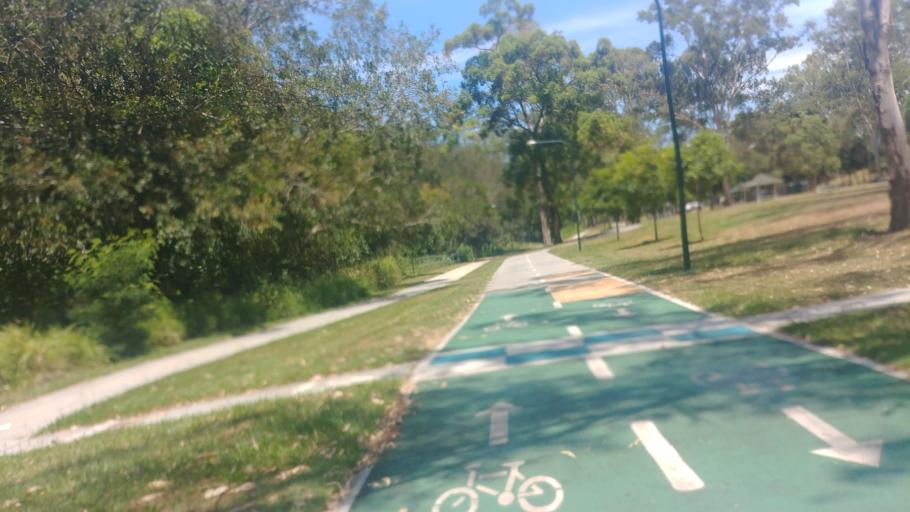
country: AU
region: Queensland
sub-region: Brisbane
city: Wavell Heights
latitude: -27.4049
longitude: 153.0509
